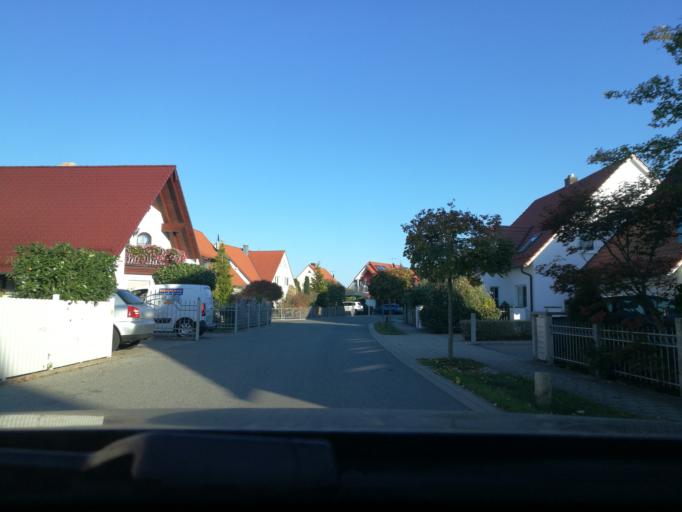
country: DE
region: Bavaria
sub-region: Regierungsbezirk Mittelfranken
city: Seukendorf
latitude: 49.4911
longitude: 10.8801
